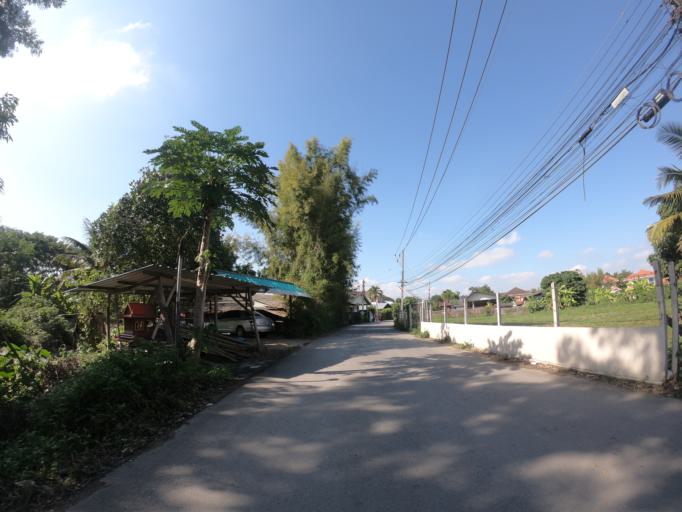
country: TH
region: Chiang Mai
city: Saraphi
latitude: 18.7133
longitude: 99.0048
